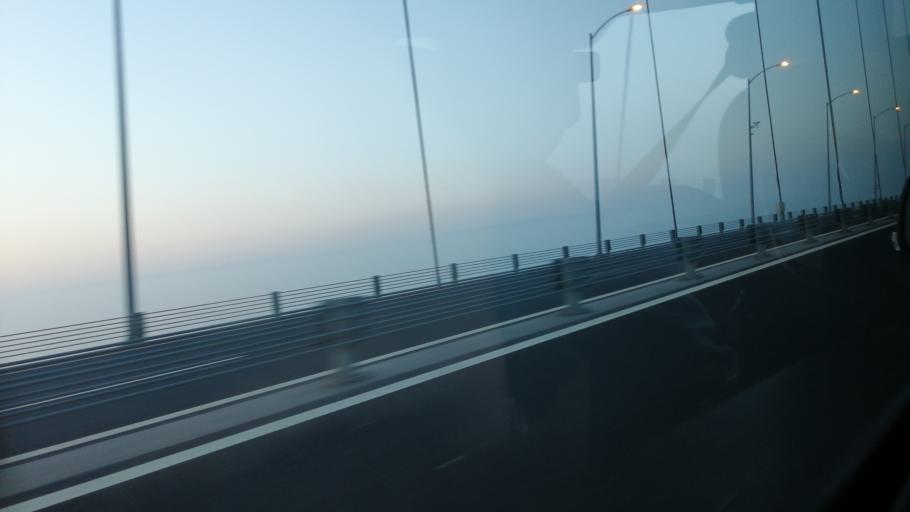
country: TR
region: Kocaeli
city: Tavsancil
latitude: 40.7575
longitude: 29.5163
